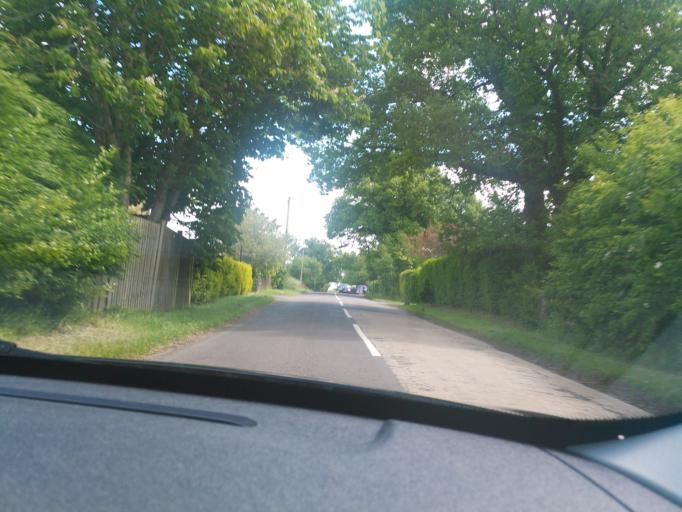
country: GB
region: England
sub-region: Shropshire
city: Prees
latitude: 52.8810
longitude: -2.6552
